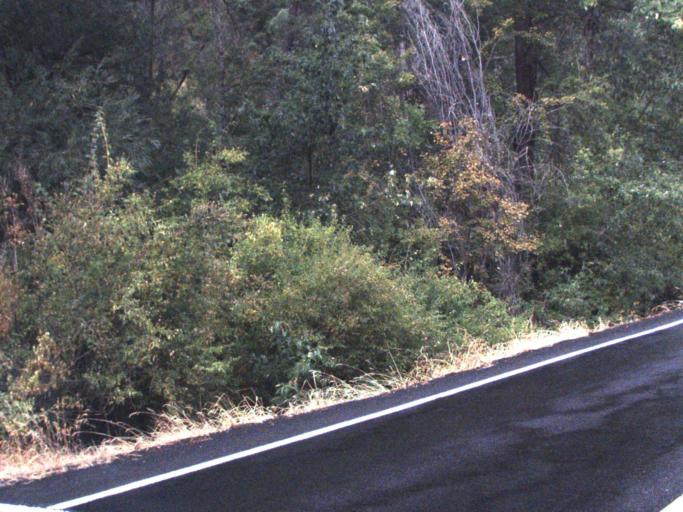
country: US
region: Washington
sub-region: Lincoln County
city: Davenport
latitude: 47.7586
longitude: -117.8910
